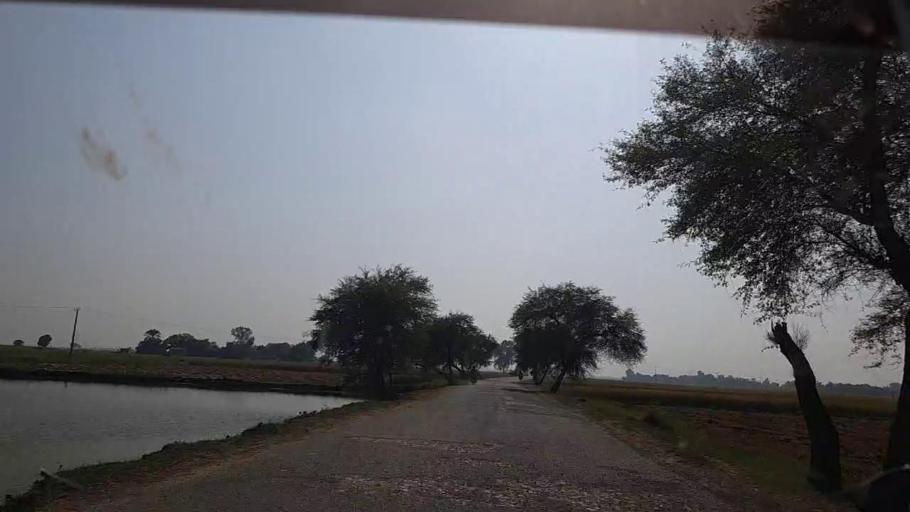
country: PK
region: Sindh
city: Shikarpur
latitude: 28.0957
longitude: 68.6101
